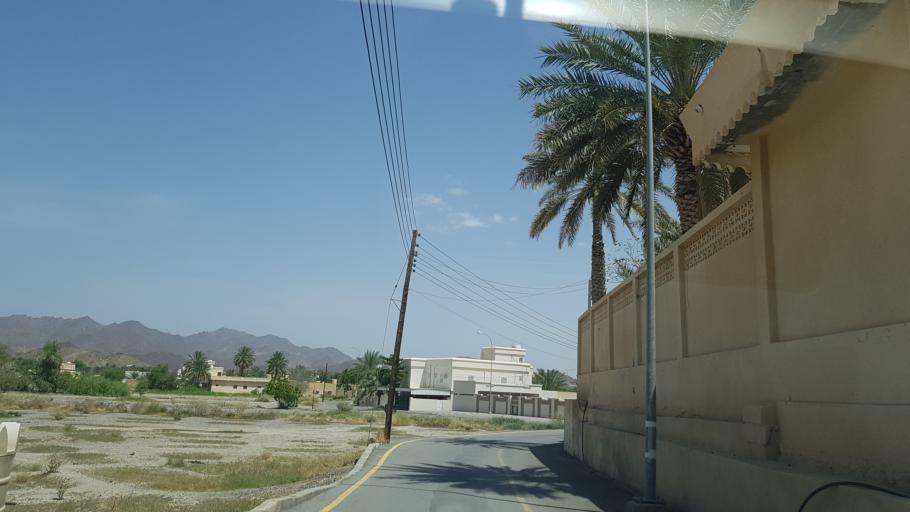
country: OM
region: Muhafazat ad Dakhiliyah
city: Bahla'
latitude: 22.9540
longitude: 57.3017
